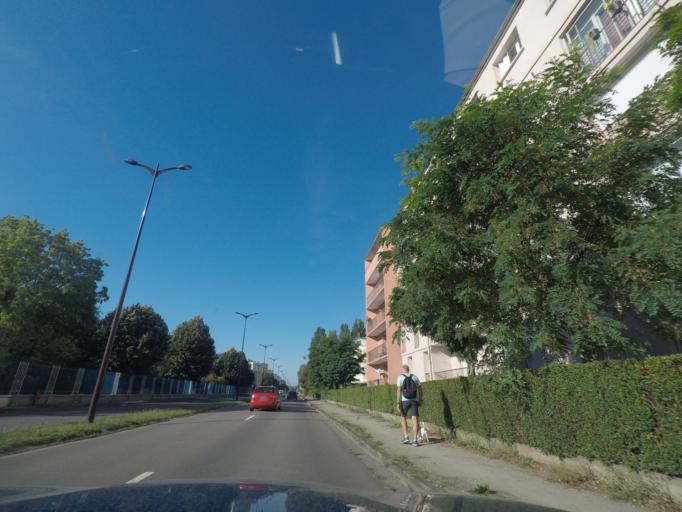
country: FR
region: Lorraine
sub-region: Departement de la Moselle
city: Thionville
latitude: 49.3695
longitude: 6.1599
